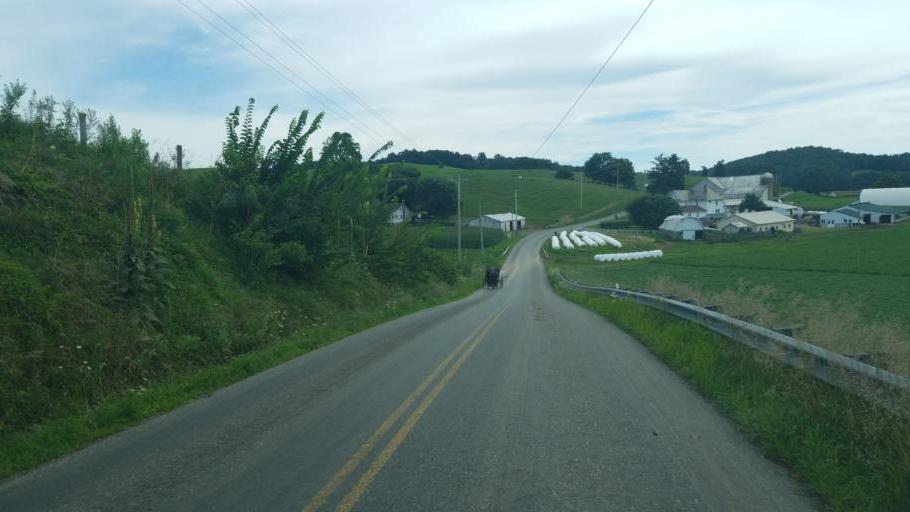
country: US
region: Ohio
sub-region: Holmes County
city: Millersburg
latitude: 40.4761
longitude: -81.8413
